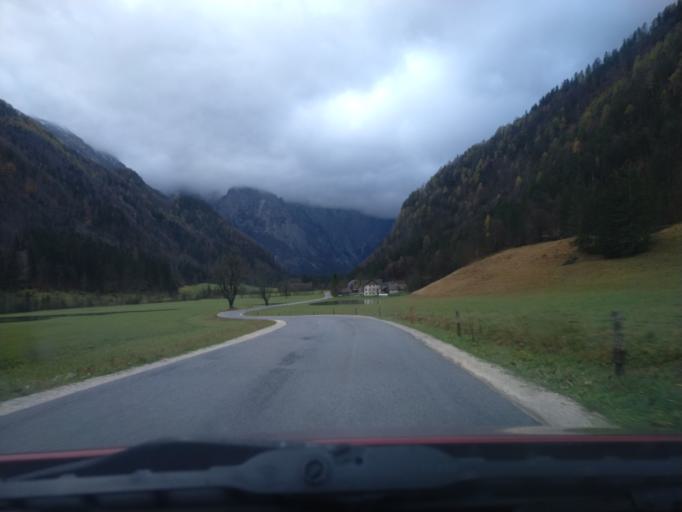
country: SI
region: Solcava
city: Solcava
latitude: 46.4177
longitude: 14.6411
